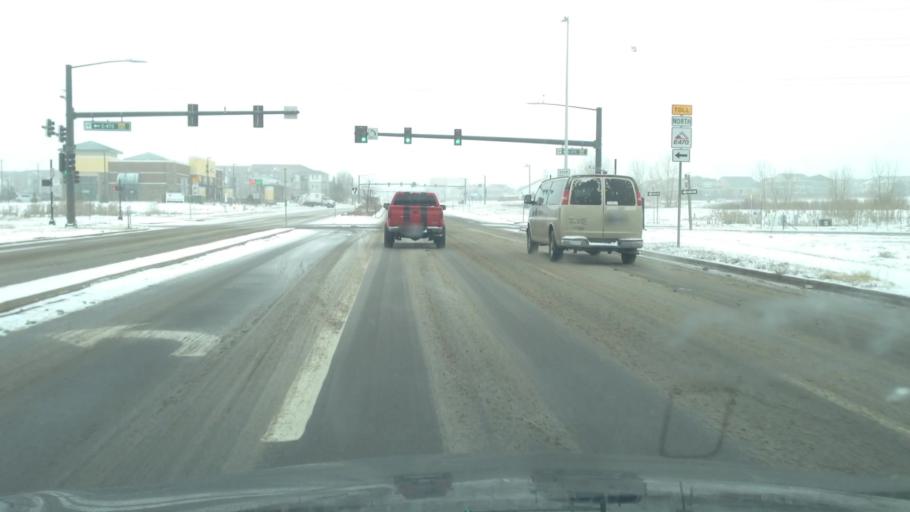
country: US
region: Colorado
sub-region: Douglas County
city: Stonegate
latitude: 39.5487
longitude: -104.7934
